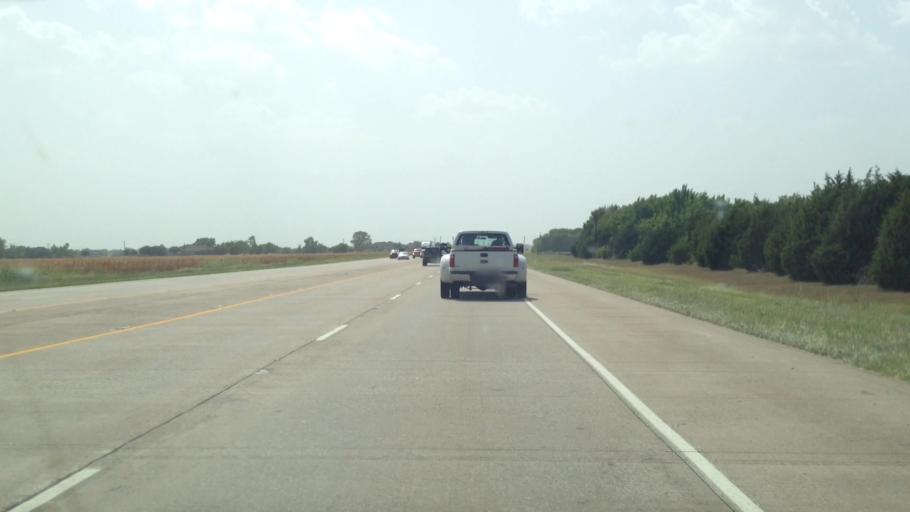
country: US
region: Texas
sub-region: Collin County
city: Princeton
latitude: 33.1648
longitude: -96.4471
